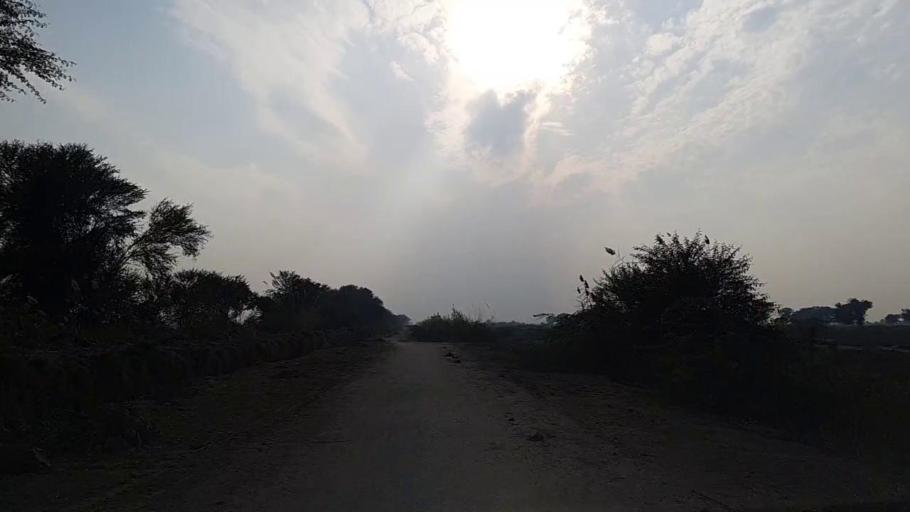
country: PK
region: Sindh
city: Jam Sahib
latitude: 26.3038
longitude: 68.5168
